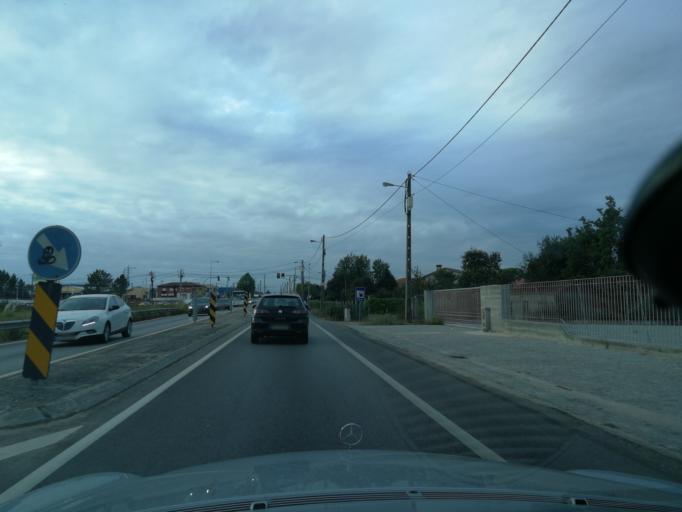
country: PT
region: Aveiro
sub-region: Agueda
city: Agueda
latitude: 40.5900
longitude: -8.4519
